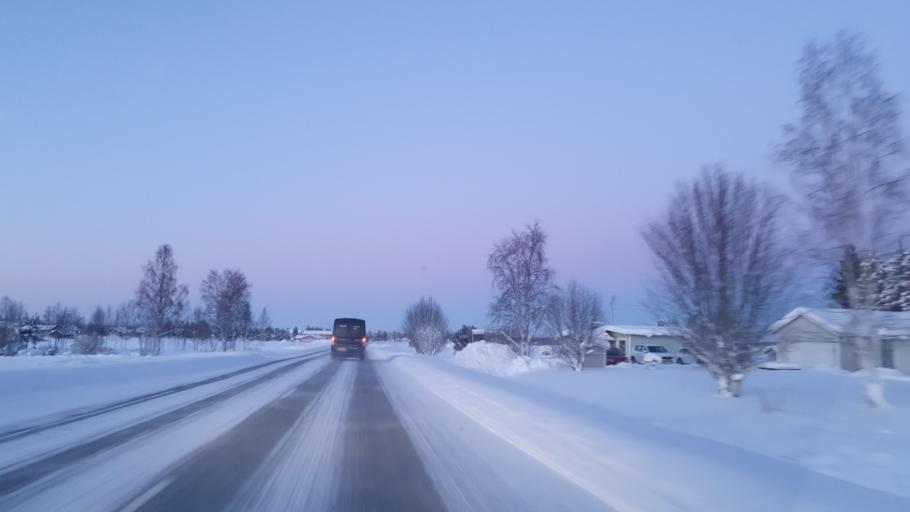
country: SE
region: Norrbotten
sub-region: Overtornea Kommun
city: OEvertornea
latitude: 66.4199
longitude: 23.6655
